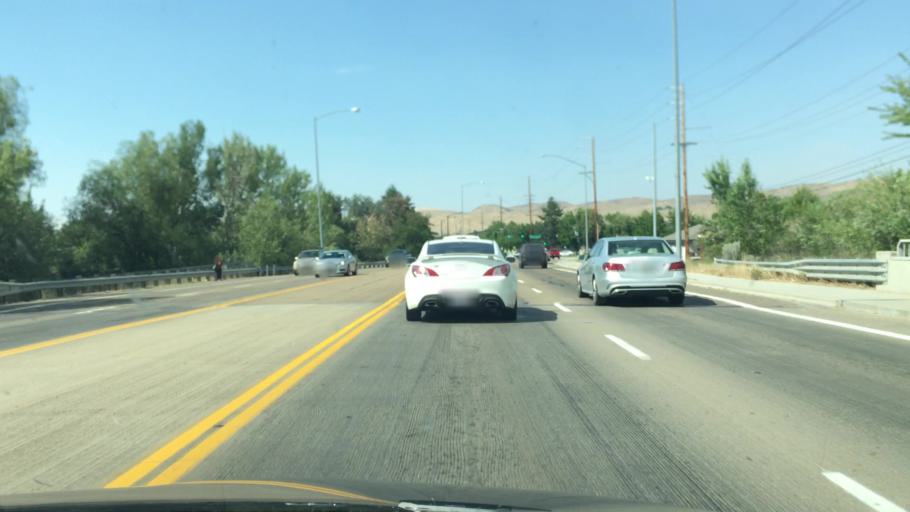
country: US
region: Idaho
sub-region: Ada County
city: Garden City
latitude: 43.6616
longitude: -116.2796
